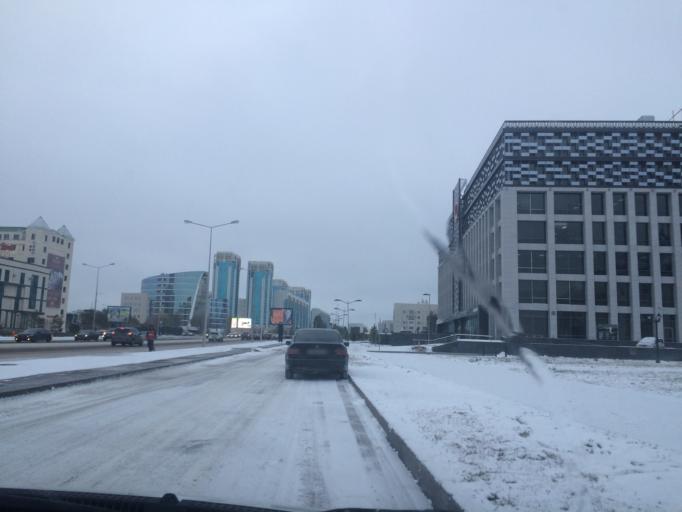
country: KZ
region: Astana Qalasy
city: Astana
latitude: 51.1366
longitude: 71.4124
